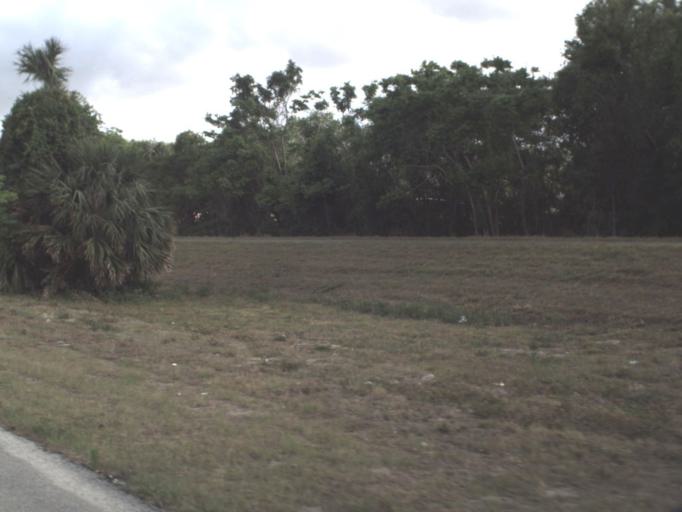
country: US
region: Florida
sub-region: Brevard County
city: Mims
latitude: 28.6473
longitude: -80.8362
